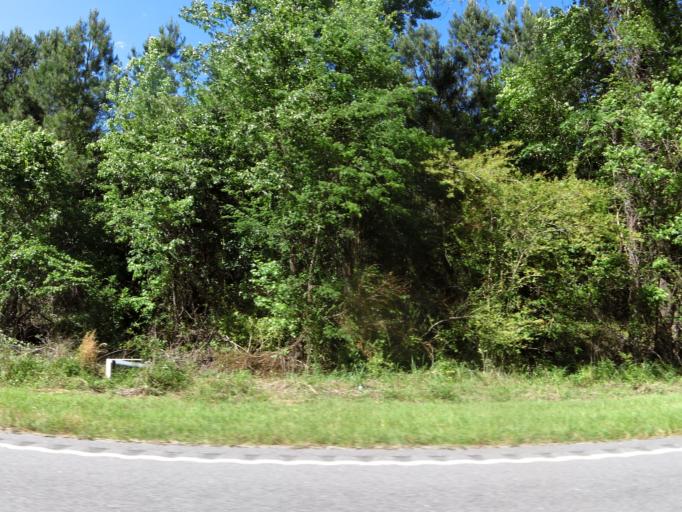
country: US
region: South Carolina
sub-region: Barnwell County
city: Blackville
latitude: 33.3657
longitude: -81.3263
